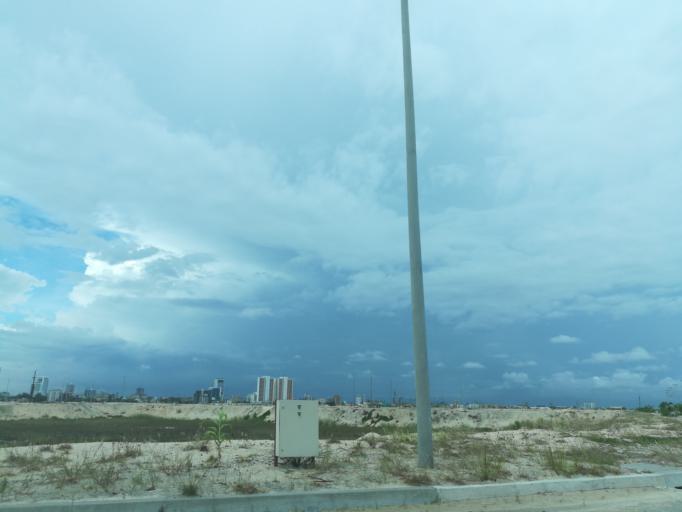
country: NG
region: Lagos
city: Ikoyi
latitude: 6.4103
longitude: 3.4200
